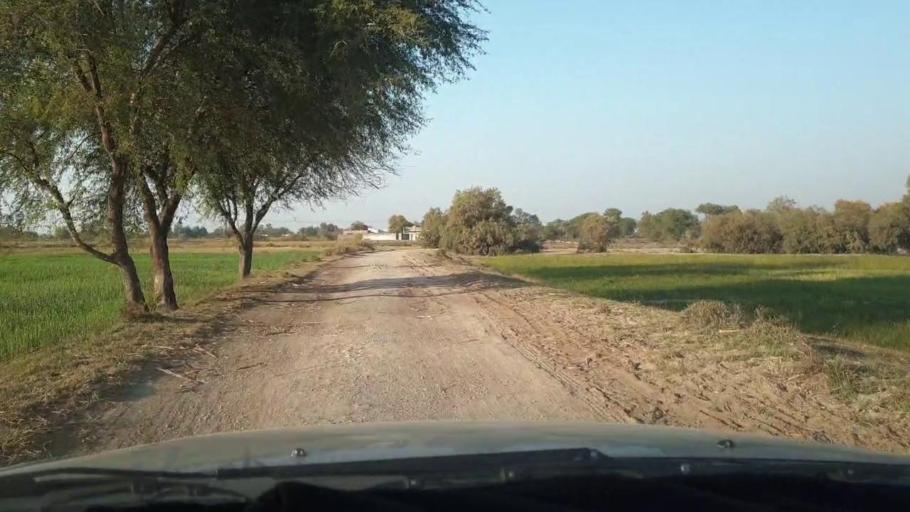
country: PK
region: Sindh
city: Mirpur Mathelo
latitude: 28.0008
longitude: 69.5037
